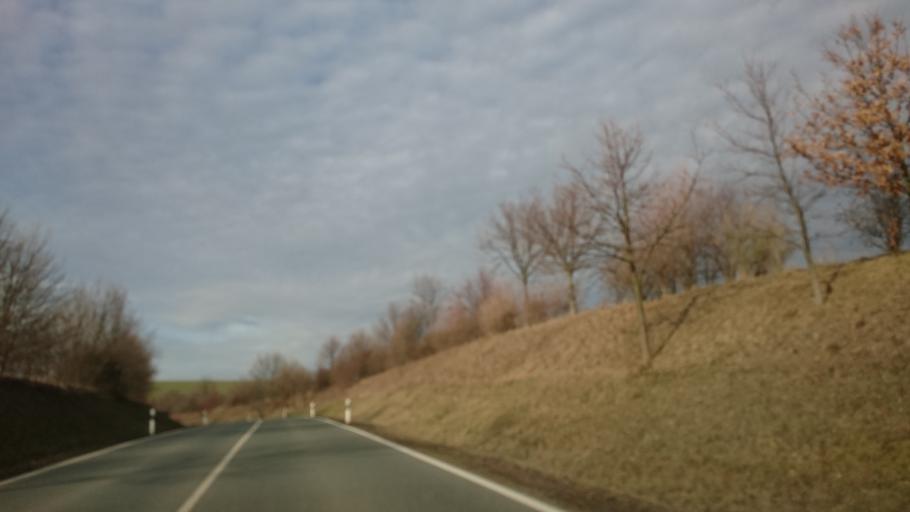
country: DE
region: Saxony
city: Sankt Egidien
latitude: 50.7899
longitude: 12.6296
